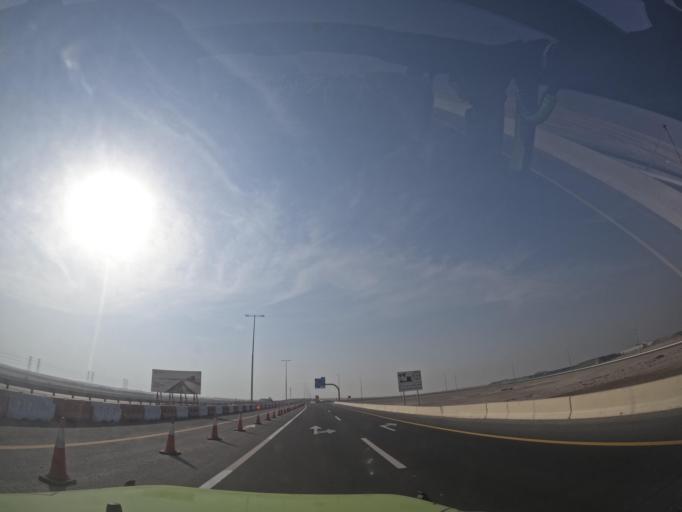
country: AE
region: Dubai
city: Dubai
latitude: 24.7919
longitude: 55.0771
